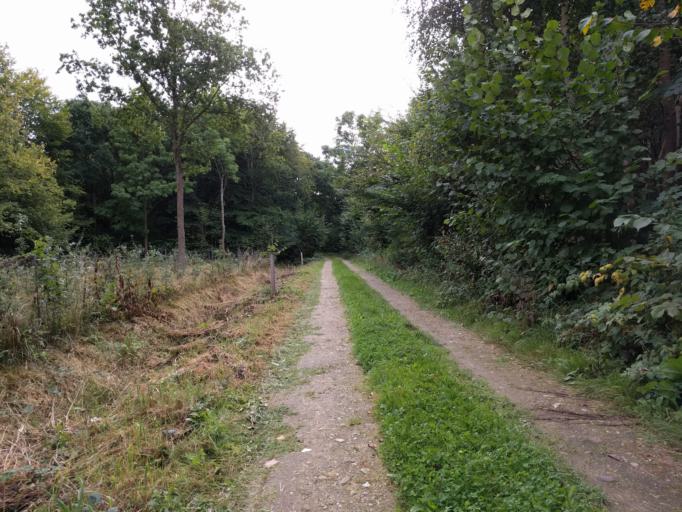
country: DK
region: South Denmark
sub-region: Kerteminde Kommune
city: Langeskov
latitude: 55.4034
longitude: 10.5647
